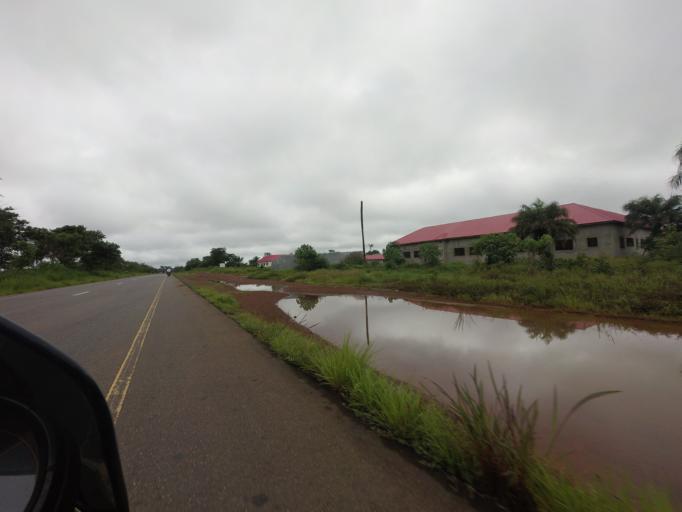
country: SL
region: Northern Province
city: Kambia
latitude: 9.0826
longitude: -12.9120
